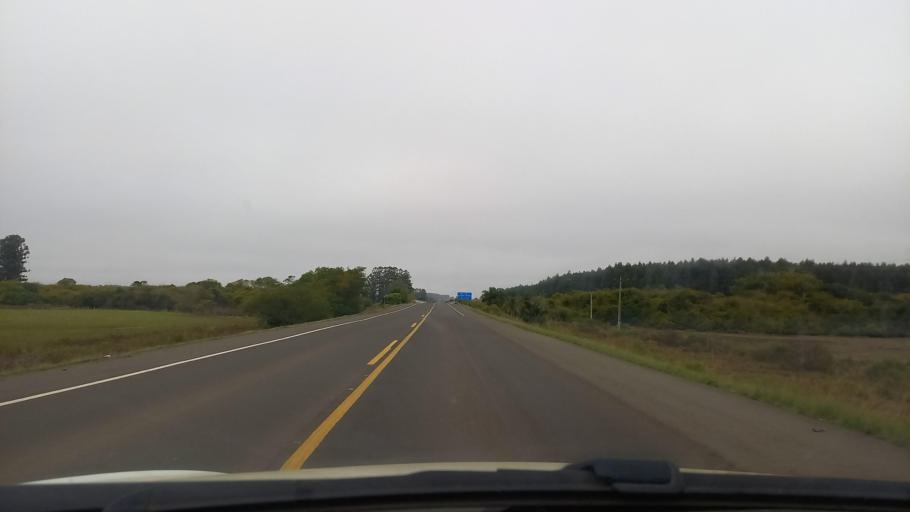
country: BR
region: Rio Grande do Sul
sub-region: Rosario Do Sul
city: Rosario do Sul
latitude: -30.2922
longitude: -54.9868
